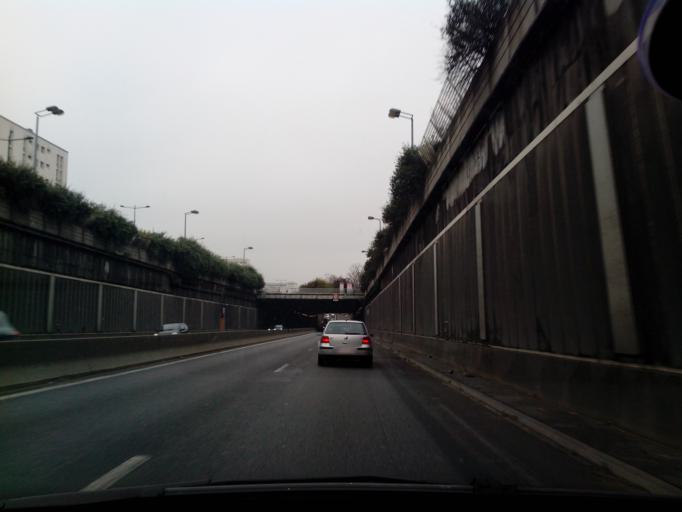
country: FR
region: Ile-de-France
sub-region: Departement du Val-de-Marne
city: Fresnes
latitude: 48.7598
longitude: 2.3220
